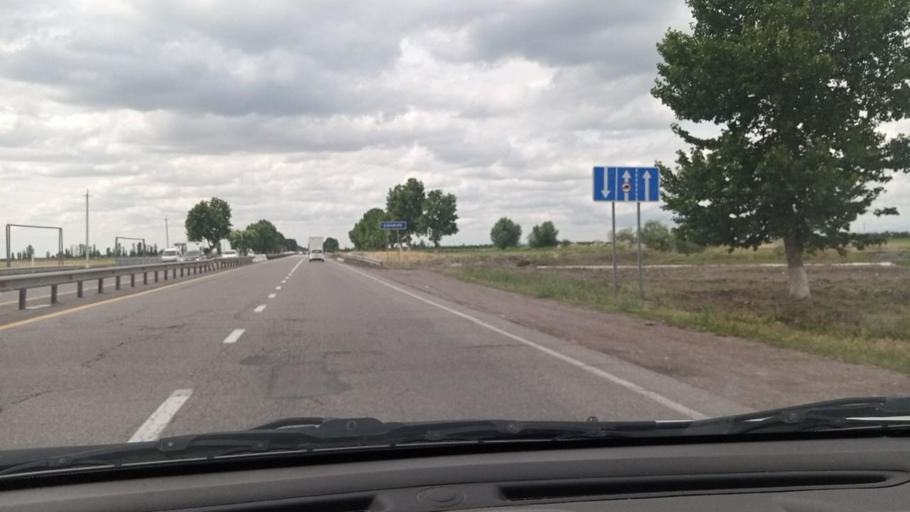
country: UZ
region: Toshkent Shahri
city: Bektemir
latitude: 41.1591
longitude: 69.4218
